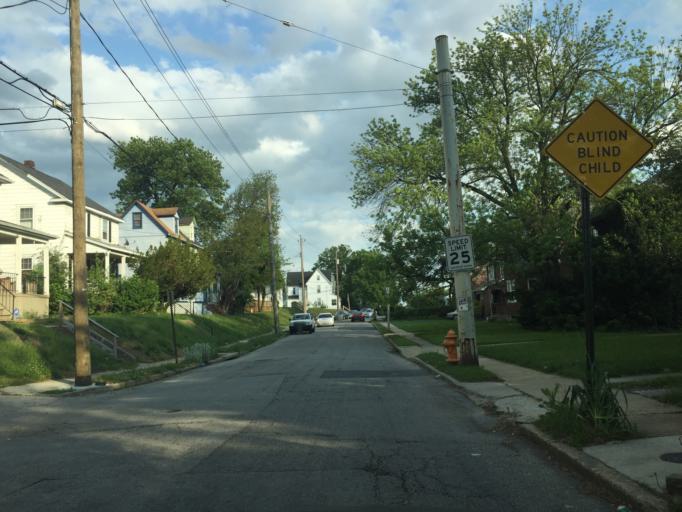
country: US
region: Maryland
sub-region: Baltimore County
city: Parkville
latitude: 39.3321
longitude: -76.5695
